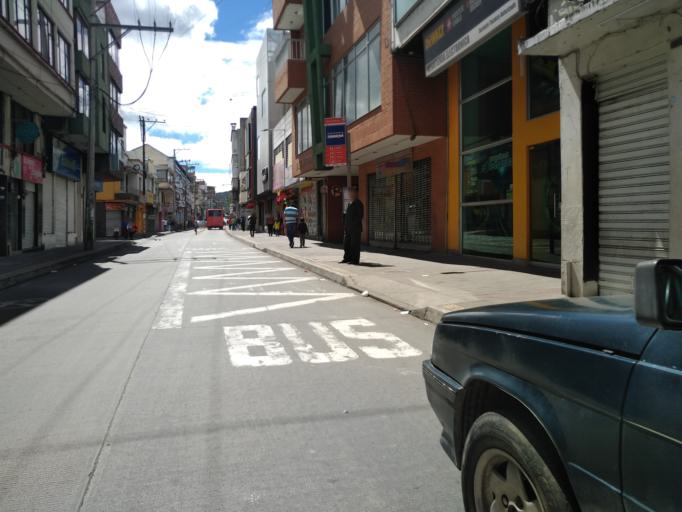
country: CO
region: Narino
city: Pasto
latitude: 1.2112
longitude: -77.2793
